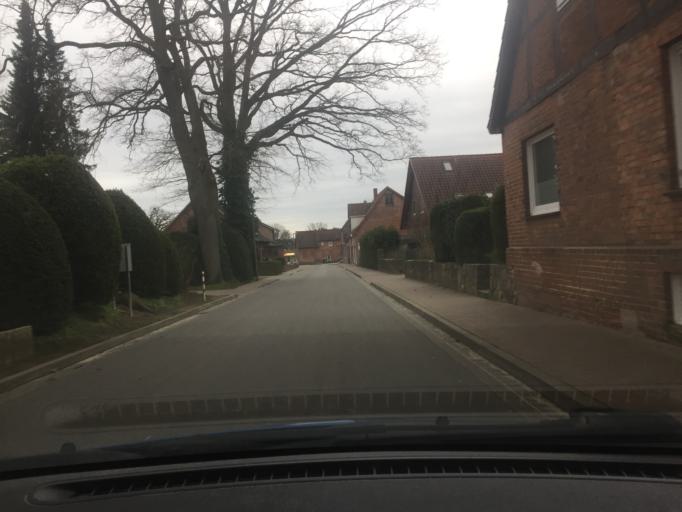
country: DE
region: Lower Saxony
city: Salzhausen
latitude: 53.2277
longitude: 10.1672
